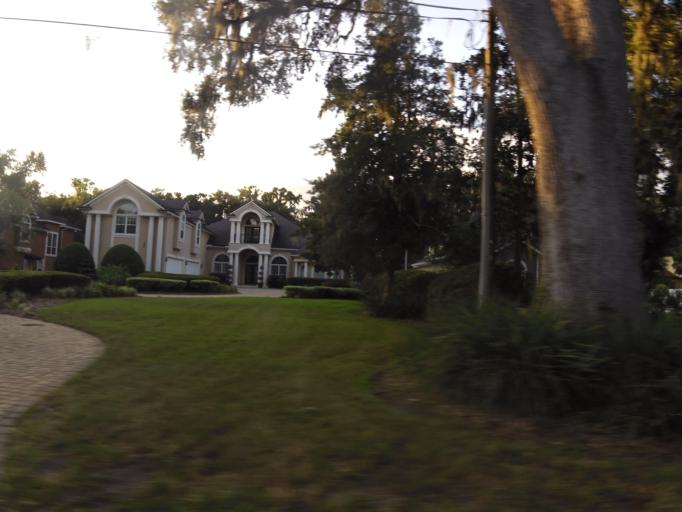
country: US
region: Florida
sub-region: Clay County
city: Orange Park
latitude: 30.2006
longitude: -81.6390
